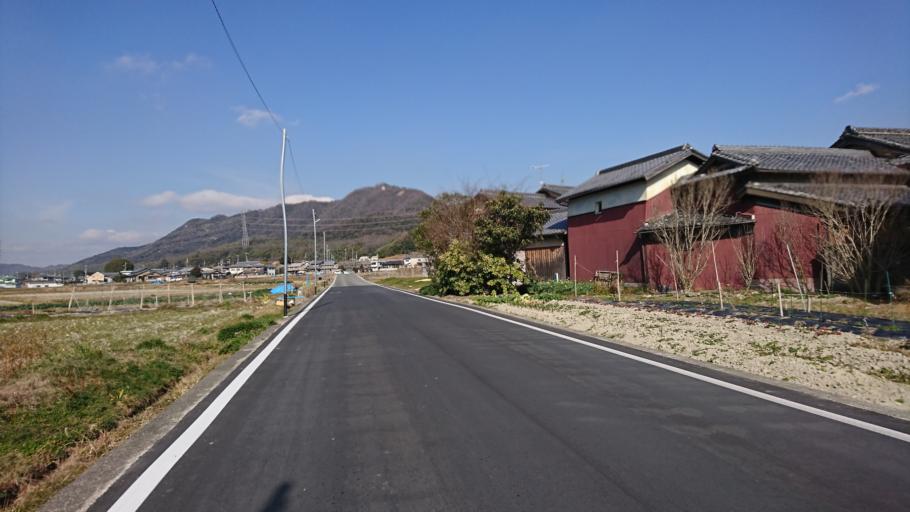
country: JP
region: Hyogo
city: Kakogawacho-honmachi
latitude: 34.8166
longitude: 134.8542
